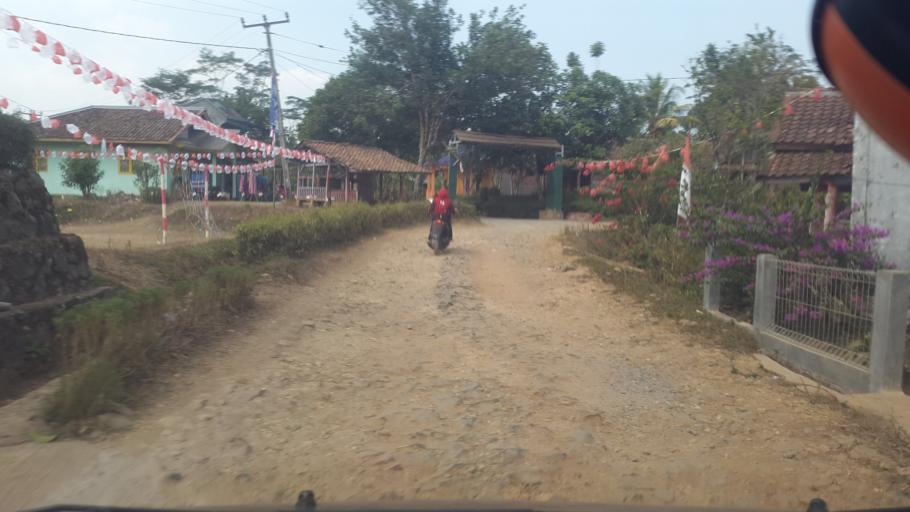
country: ID
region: West Java
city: Nangerang
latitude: -7.1113
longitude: 106.7873
